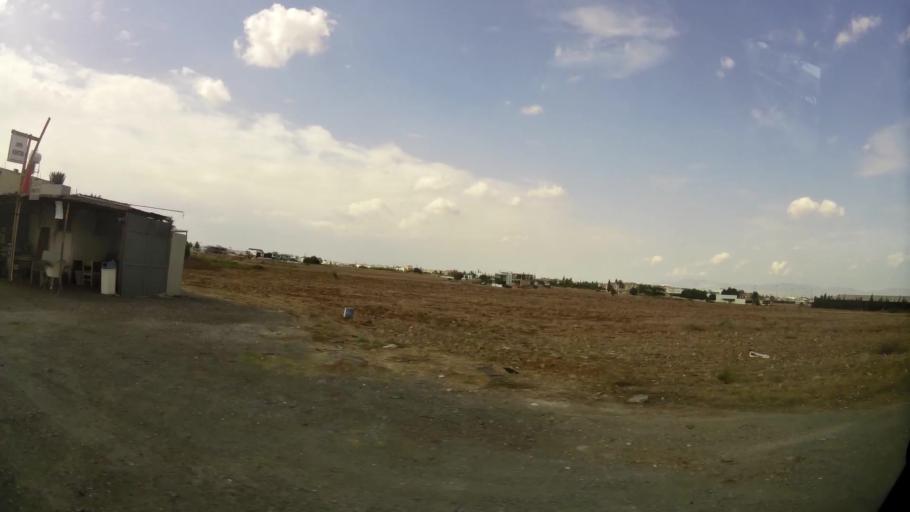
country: CY
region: Lefkosia
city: Tseri
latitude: 35.1069
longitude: 33.3305
